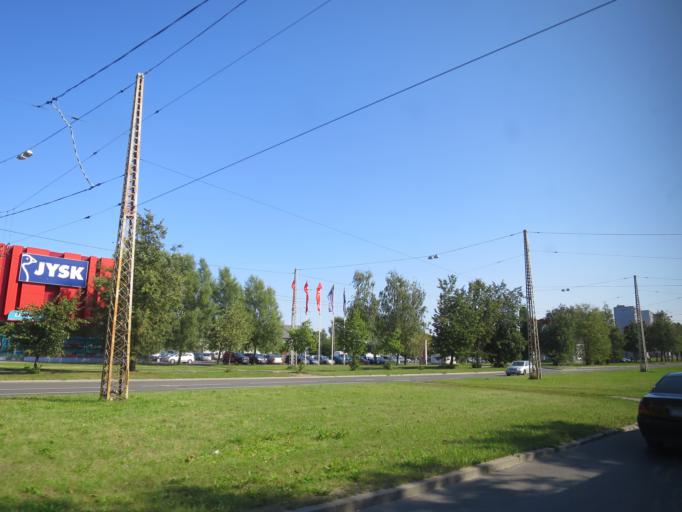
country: LV
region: Riga
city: Riga
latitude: 56.9576
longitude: 24.1852
